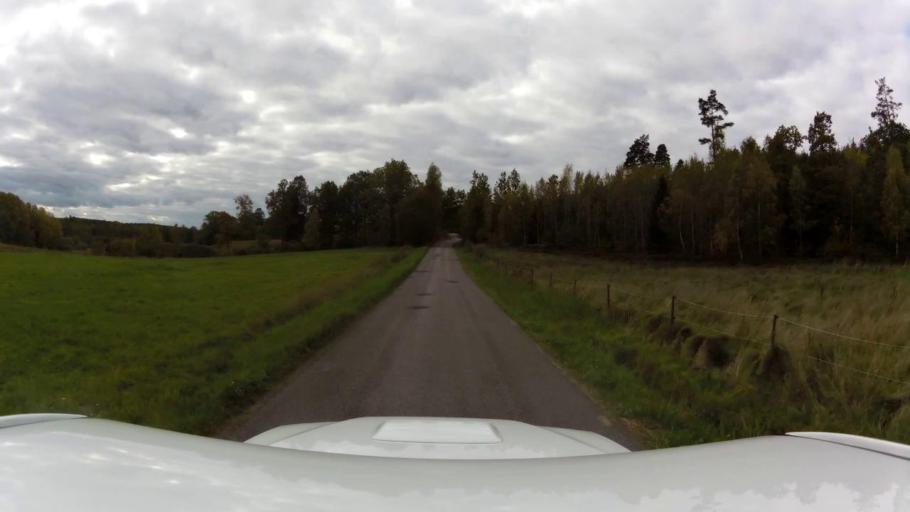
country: SE
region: OEstergoetland
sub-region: Kinda Kommun
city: Rimforsa
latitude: 58.2333
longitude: 15.6283
